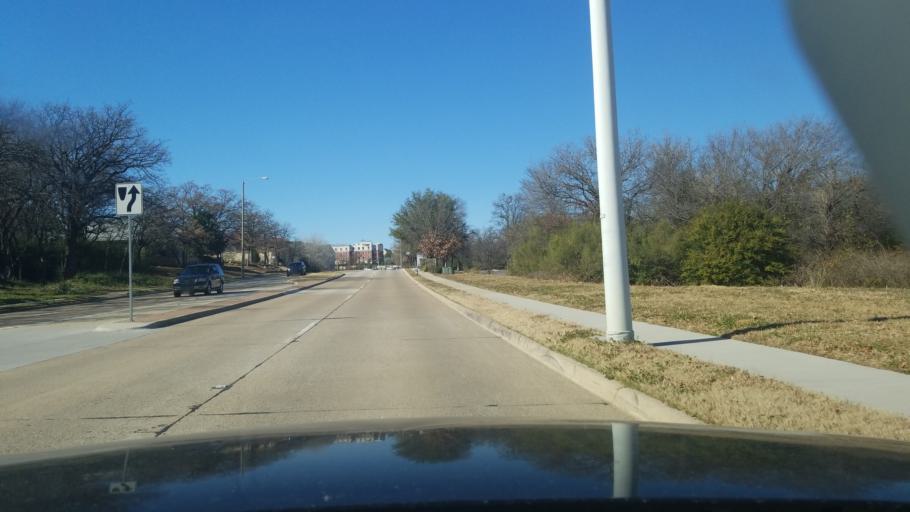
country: US
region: Texas
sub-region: Denton County
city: Corinth
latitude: 33.1812
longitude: -97.0947
